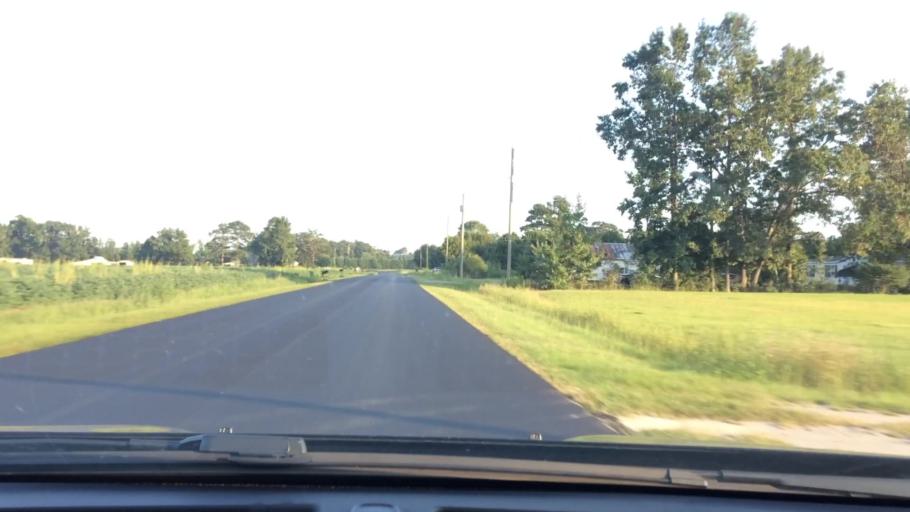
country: US
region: North Carolina
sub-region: Pitt County
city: Ayden
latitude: 35.4556
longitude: -77.4686
